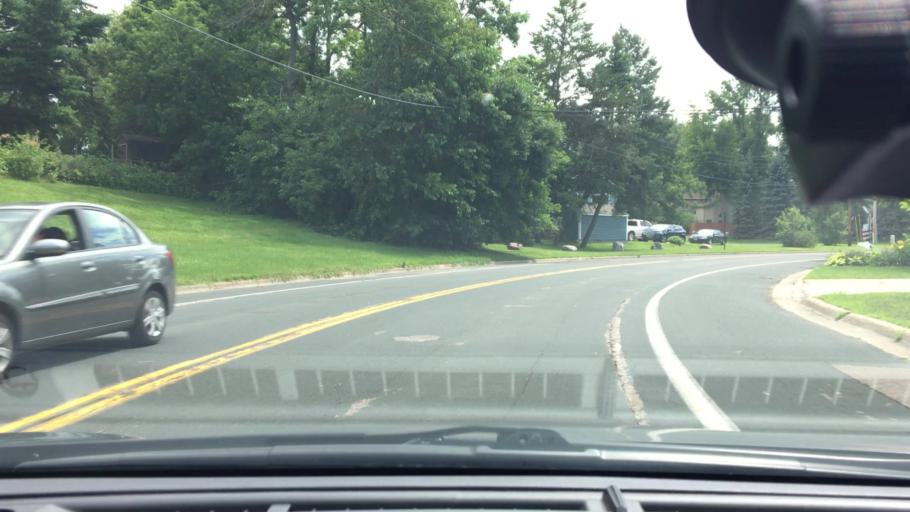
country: US
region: Minnesota
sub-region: Hennepin County
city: New Hope
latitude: 45.0084
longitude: -93.4088
